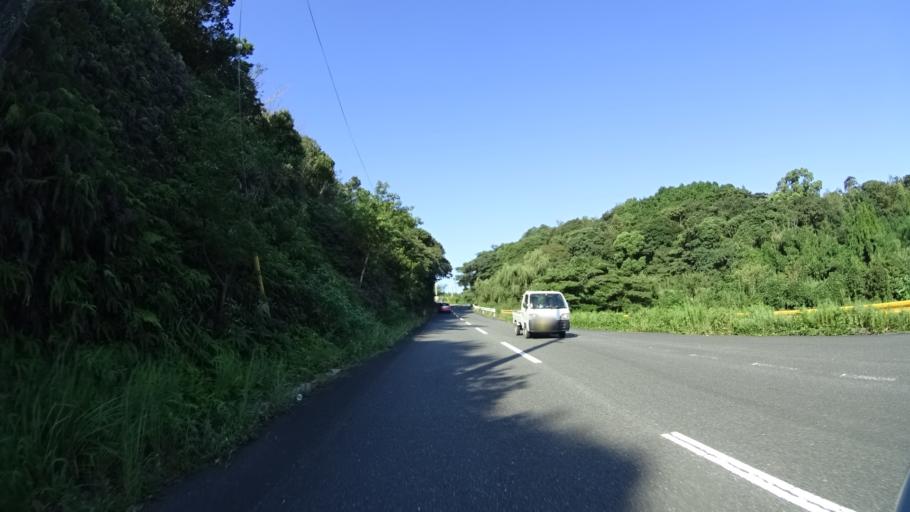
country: JP
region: Yamaguchi
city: Nagato
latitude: 34.3417
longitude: 130.9026
